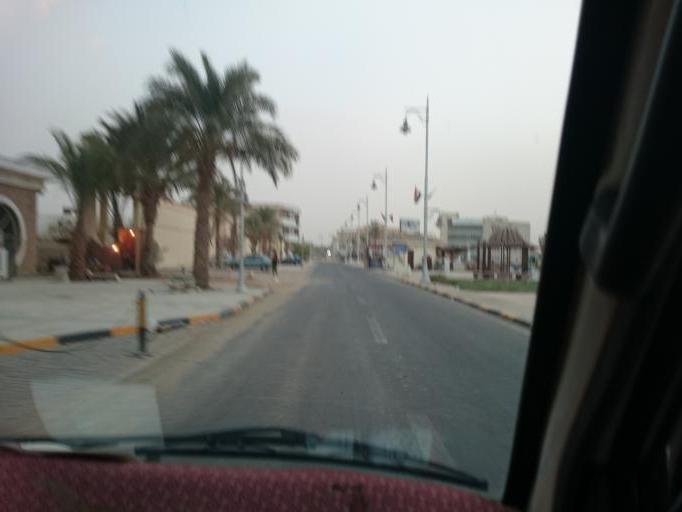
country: EG
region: Red Sea
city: Hurghada
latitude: 27.1835
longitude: 33.8249
